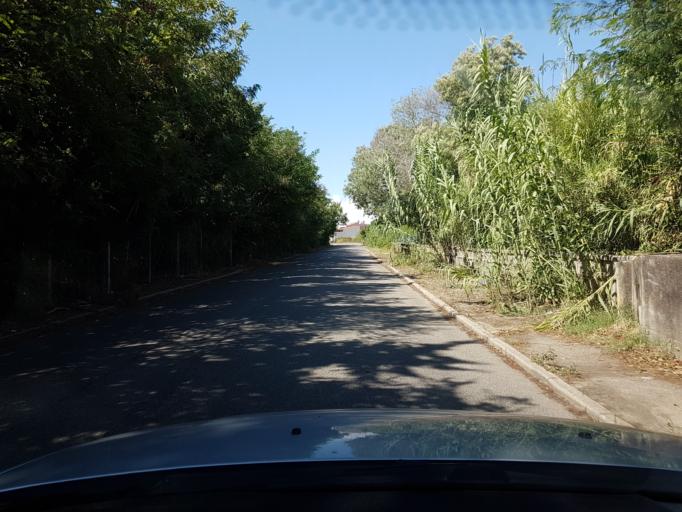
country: IT
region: Sardinia
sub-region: Provincia di Oristano
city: Donigala Fenugheddu
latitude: 39.9300
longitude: 8.5733
